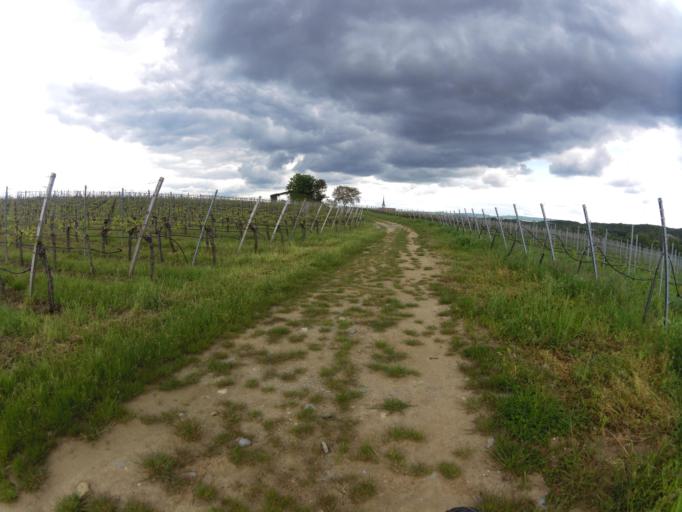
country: DE
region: Bavaria
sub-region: Regierungsbezirk Unterfranken
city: Sommerach
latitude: 49.8329
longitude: 10.1964
